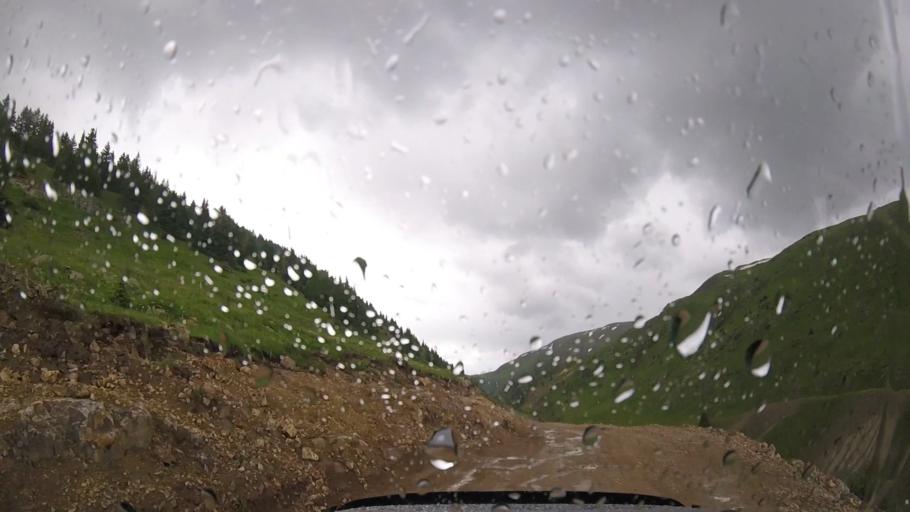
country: US
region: Colorado
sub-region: Ouray County
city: Ouray
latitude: 37.9456
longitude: -107.5742
